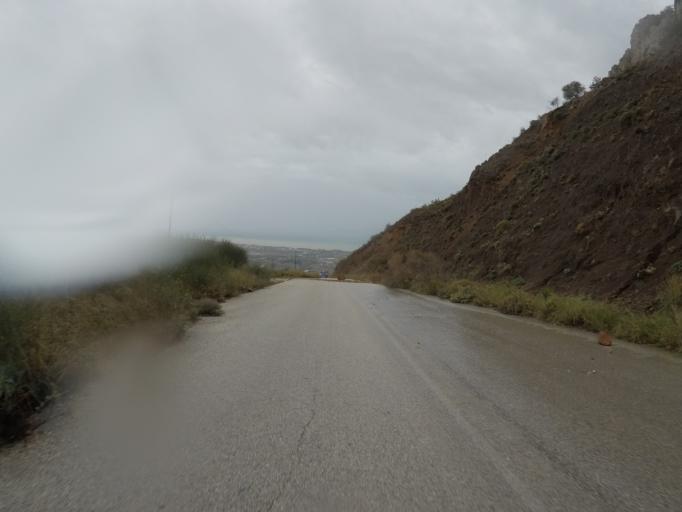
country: GR
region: Peloponnese
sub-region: Nomos Korinthias
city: Arkhaia Korinthos
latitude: 37.8919
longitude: 22.8683
